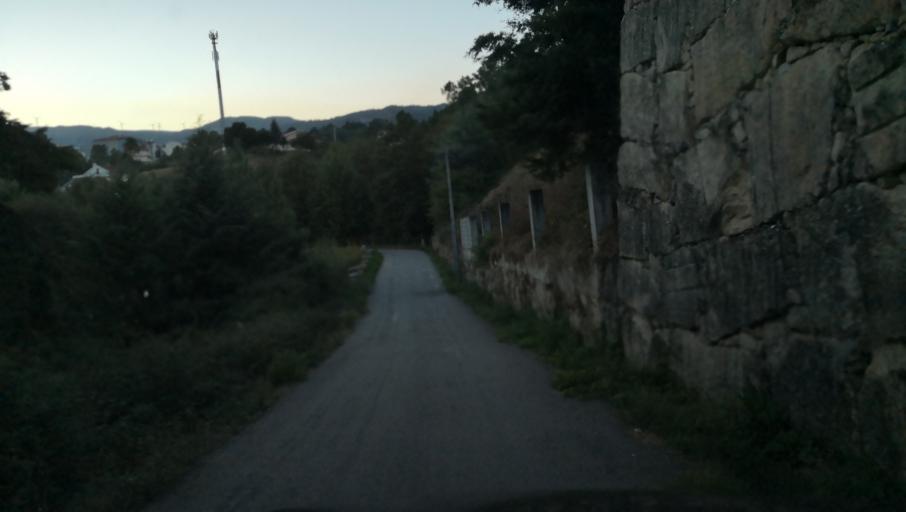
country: PT
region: Vila Real
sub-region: Vila Real
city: Vila Real
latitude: 41.3085
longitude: -7.7617
